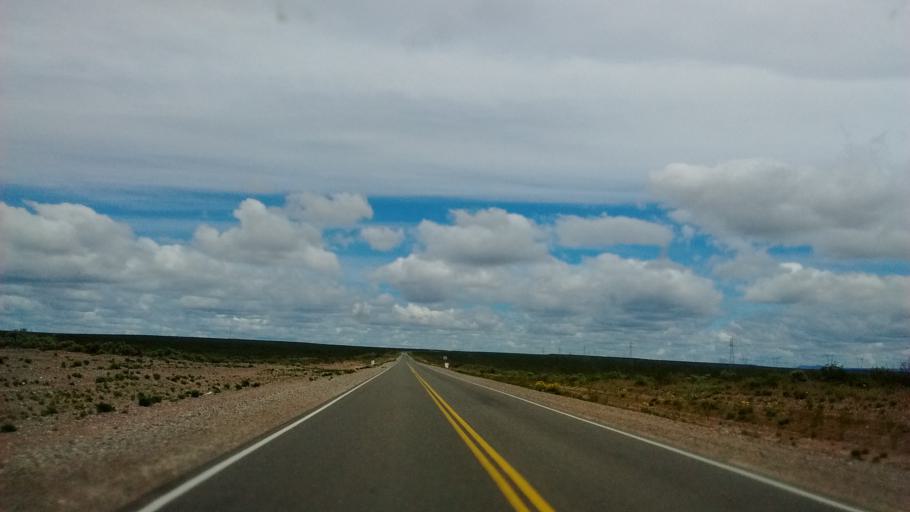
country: AR
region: Neuquen
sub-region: Departamento de Picun Leufu
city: Picun Leufu
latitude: -39.7385
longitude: -69.5962
